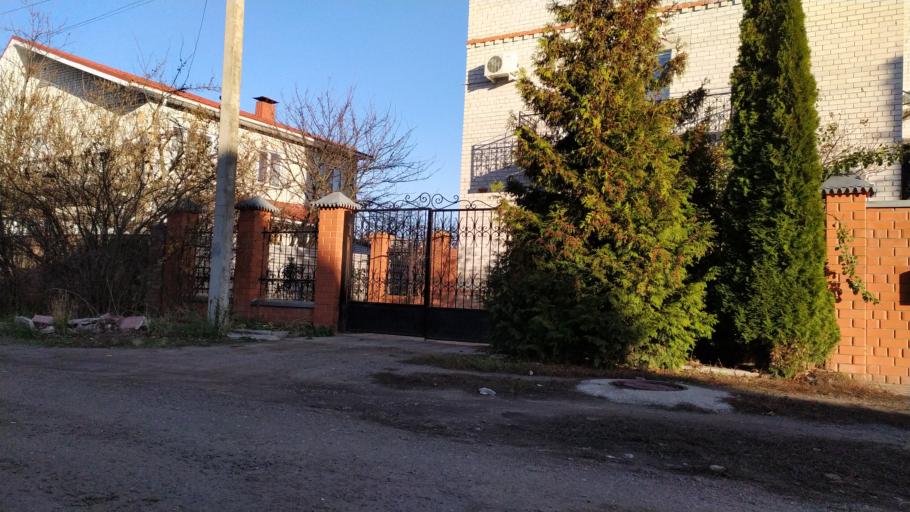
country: RU
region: Kursk
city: Kursk
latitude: 51.6456
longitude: 36.1379
